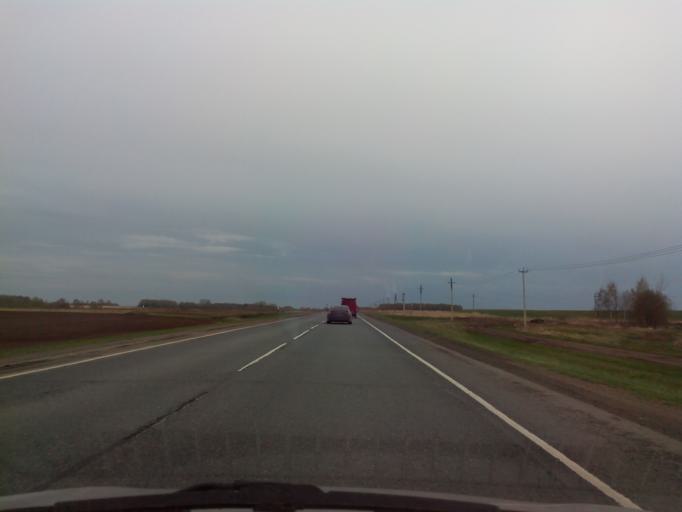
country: RU
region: Moskovskaya
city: Ozherel'ye
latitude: 54.6442
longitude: 38.3666
